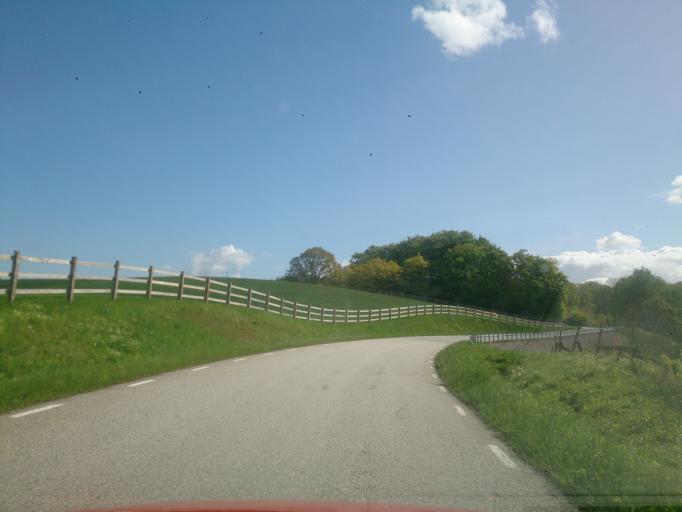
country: SE
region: Skane
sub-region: Sjobo Kommun
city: Sjoebo
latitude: 55.5520
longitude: 13.7138
